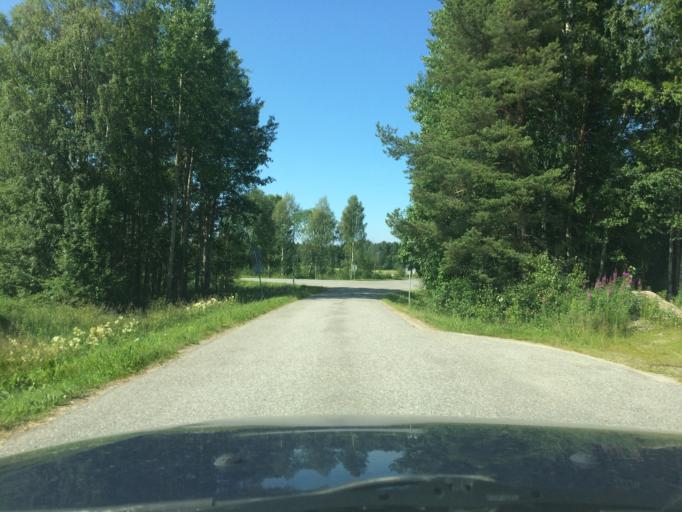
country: SE
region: Norrbotten
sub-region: Pitea Kommun
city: Norrfjarden
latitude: 65.3658
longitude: 21.4122
